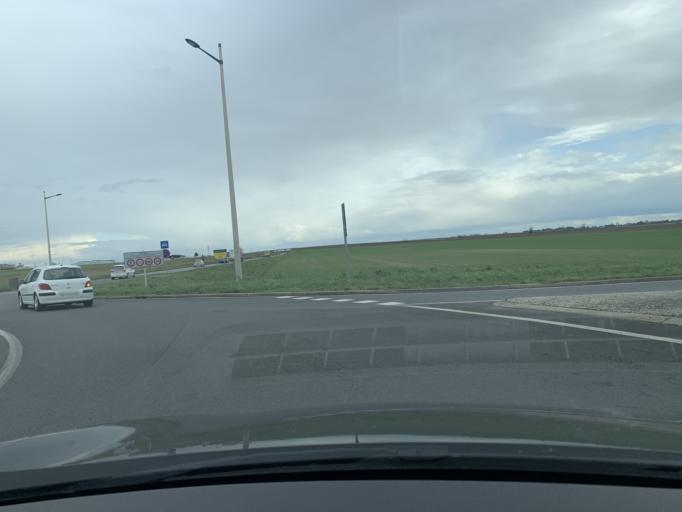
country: FR
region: Nord-Pas-de-Calais
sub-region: Departement du Nord
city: Proville
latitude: 50.1480
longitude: 3.2015
